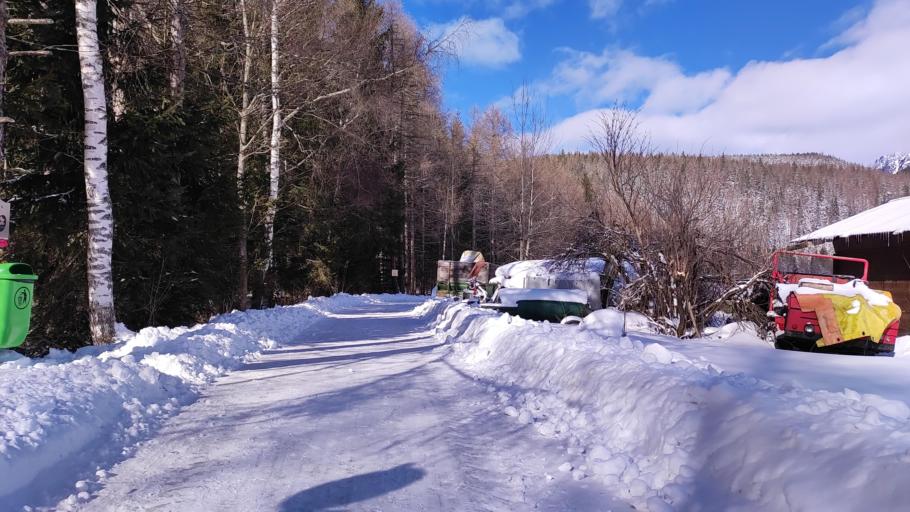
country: AT
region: Tyrol
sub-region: Politischer Bezirk Imst
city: Umhausen
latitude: 47.0983
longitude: 10.9376
